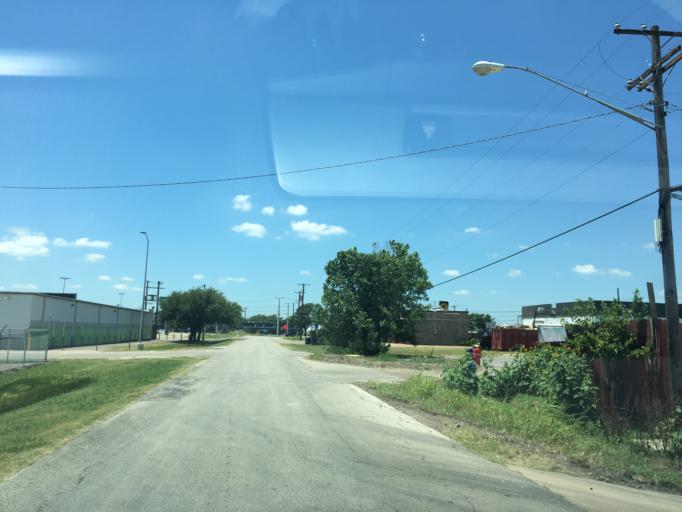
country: US
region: Texas
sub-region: Dallas County
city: Garland
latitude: 32.8453
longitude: -96.6864
